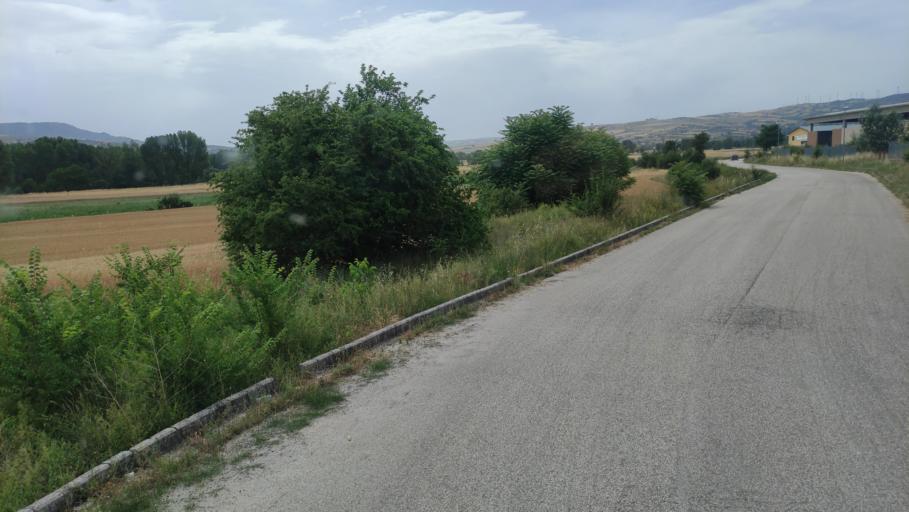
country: IT
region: Campania
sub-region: Provincia di Avellino
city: Sturno
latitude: 41.0488
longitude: 15.1294
